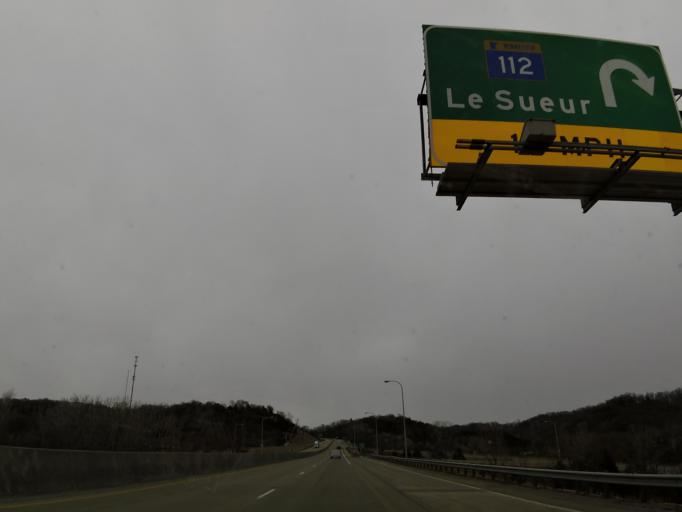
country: US
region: Minnesota
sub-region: Le Sueur County
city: Le Sueur
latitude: 44.4817
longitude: -93.8979
